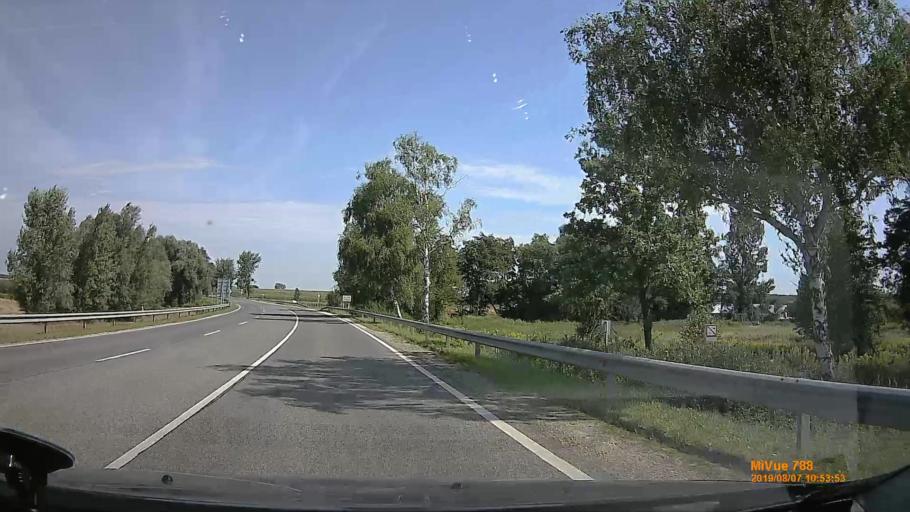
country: SI
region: Lendava-Lendva
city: Lendava
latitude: 46.6025
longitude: 16.4631
